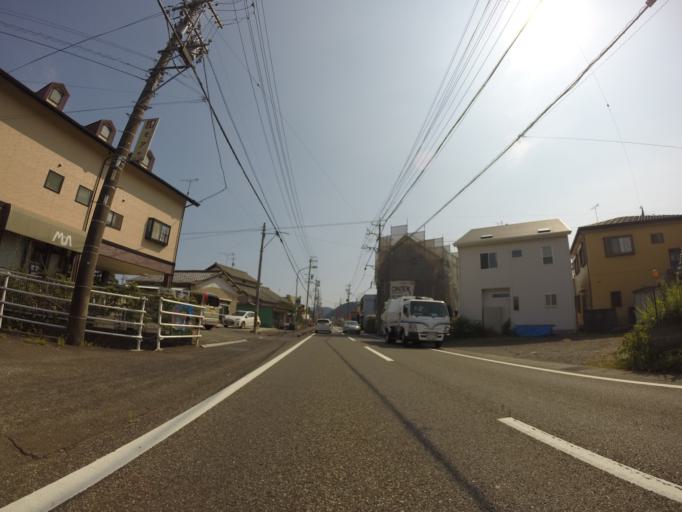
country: JP
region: Shizuoka
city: Shizuoka-shi
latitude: 35.0203
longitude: 138.3602
